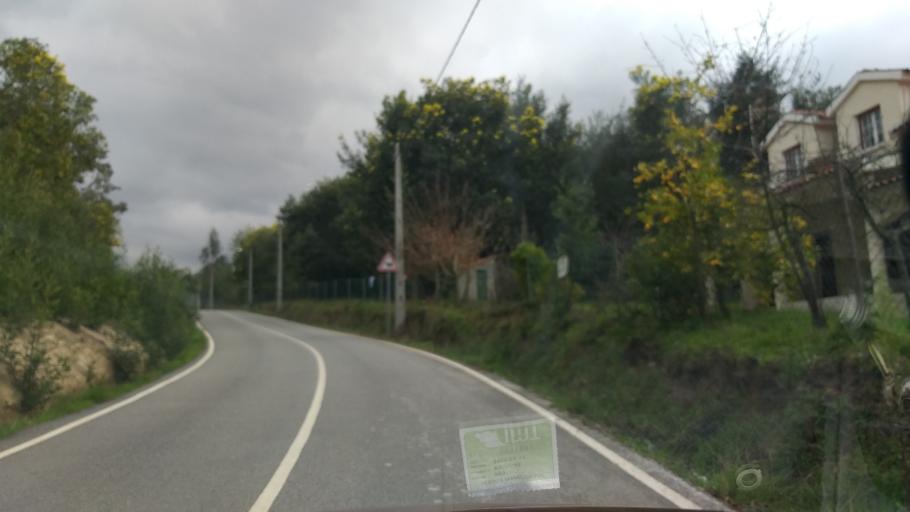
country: PT
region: Guarda
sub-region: Seia
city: Seia
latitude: 40.4793
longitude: -7.6656
